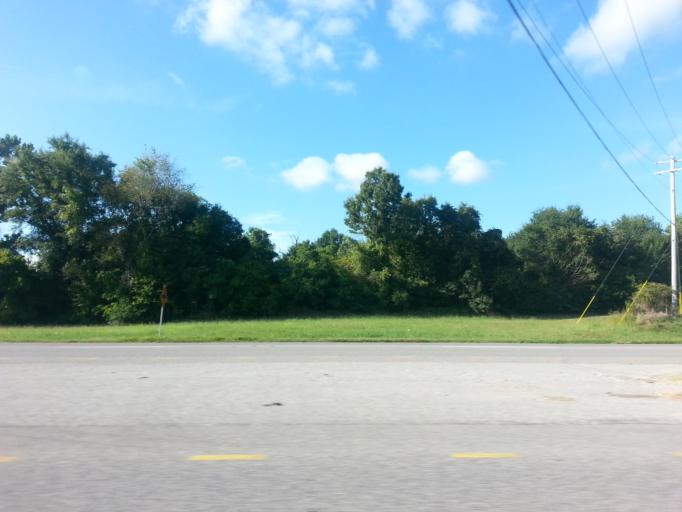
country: US
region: Alabama
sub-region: Colbert County
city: Tuscumbia
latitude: 34.7095
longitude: -87.7477
